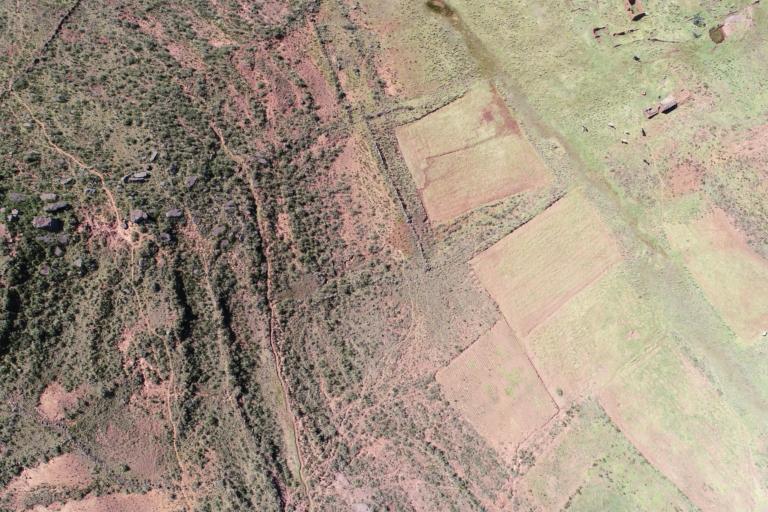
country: BO
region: La Paz
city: Tiahuanaco
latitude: -16.6068
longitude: -68.7753
